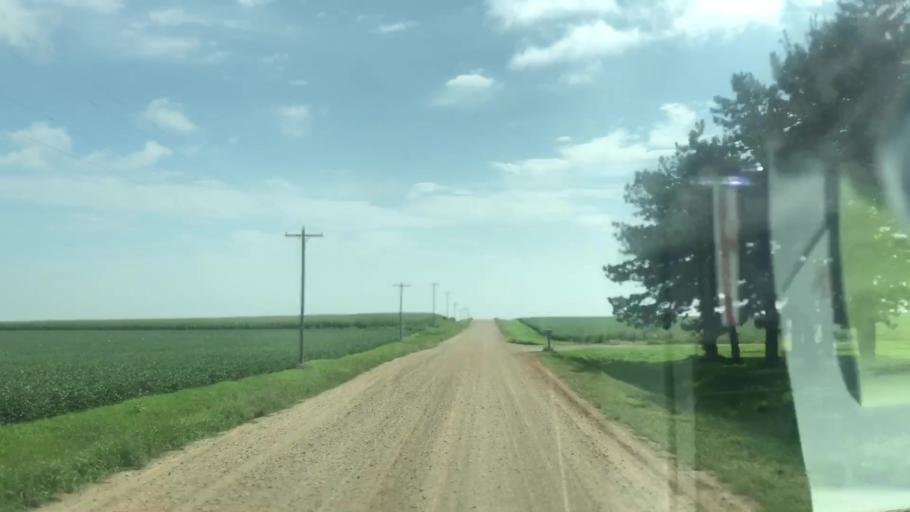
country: US
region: Iowa
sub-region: O'Brien County
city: Sheldon
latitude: 43.2153
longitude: -95.9785
